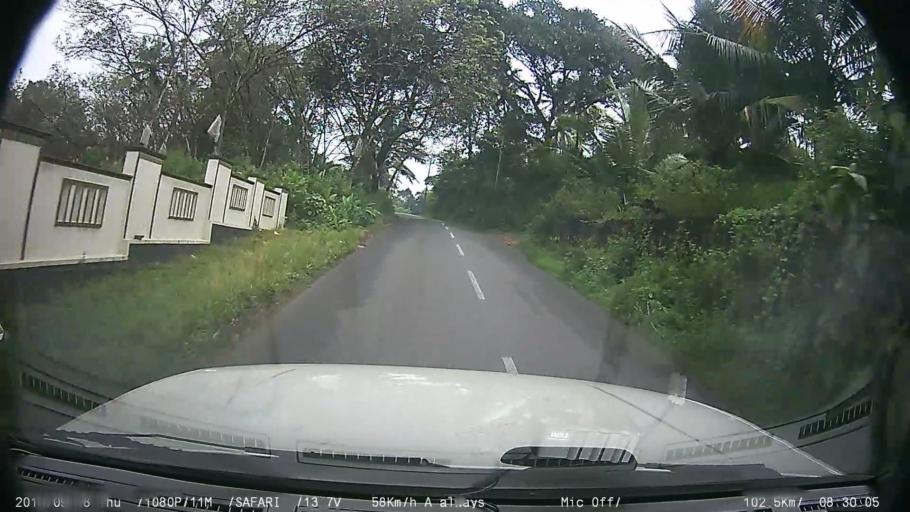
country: IN
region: Kerala
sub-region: Kottayam
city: Palackattumala
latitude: 9.6906
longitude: 76.6095
